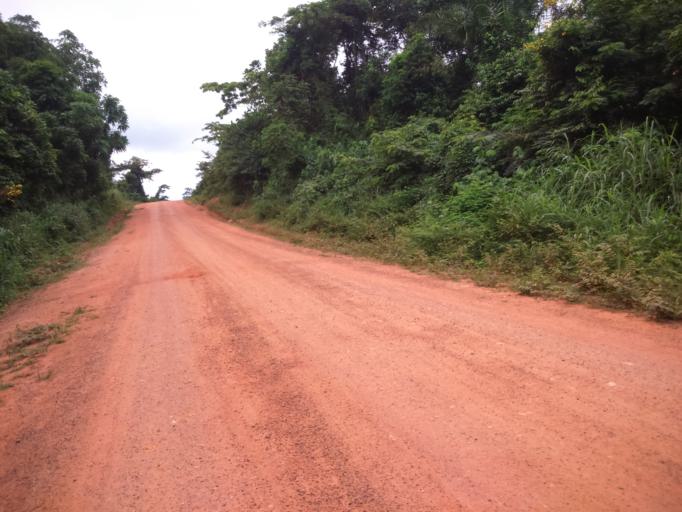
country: CI
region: Lagunes
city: Agou
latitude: 6.0814
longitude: -4.0670
